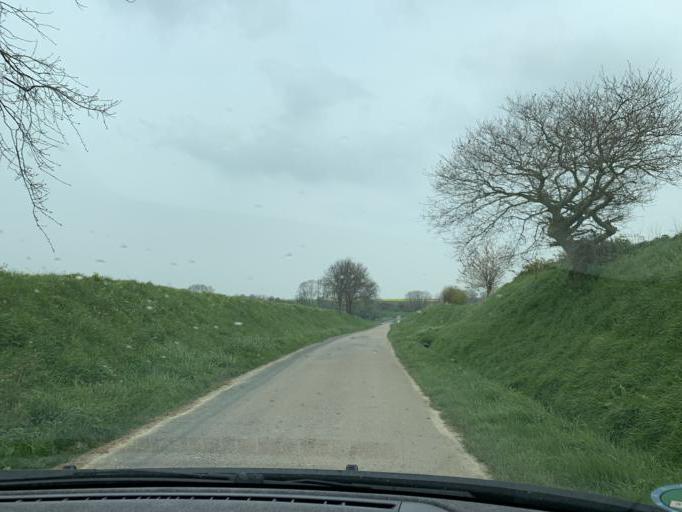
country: FR
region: Haute-Normandie
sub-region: Departement de la Seine-Maritime
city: Fontaine-le-Dun
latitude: 49.8567
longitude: 0.8150
